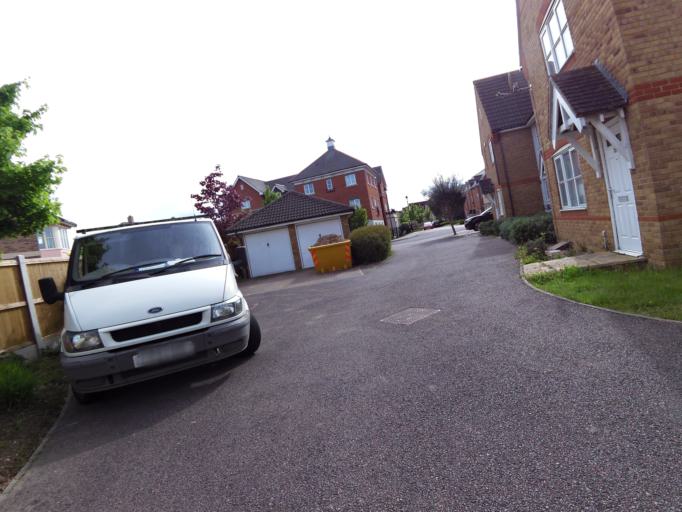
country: GB
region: England
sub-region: Suffolk
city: Ipswich
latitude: 52.0321
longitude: 1.1966
